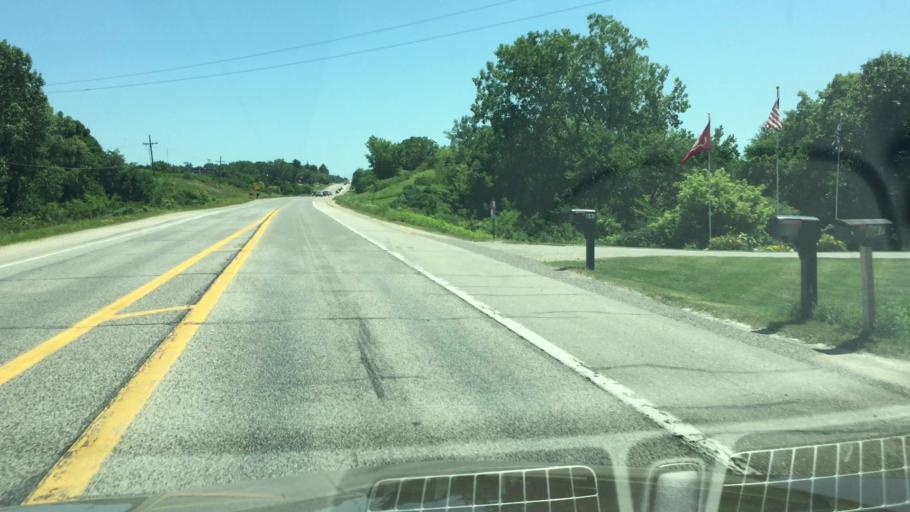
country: US
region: Iowa
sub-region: Linn County
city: Lisbon
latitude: 41.9176
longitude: -91.3979
